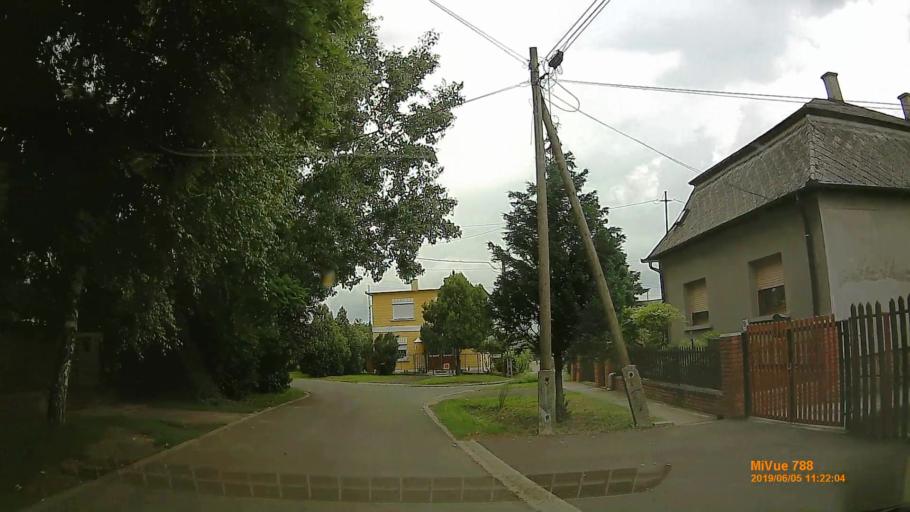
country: HU
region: Pest
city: Maglod
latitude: 47.4412
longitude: 19.3453
